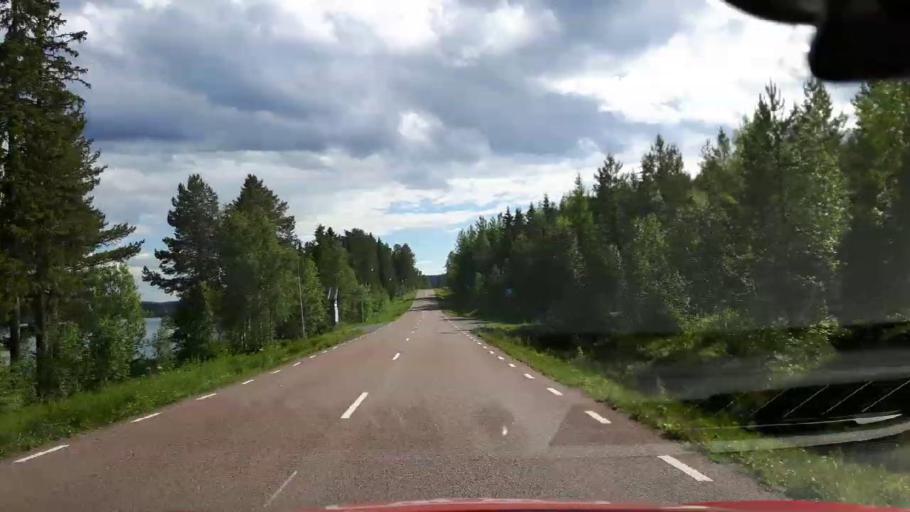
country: SE
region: Jaemtland
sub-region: Krokoms Kommun
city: Valla
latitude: 63.9817
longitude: 14.2218
